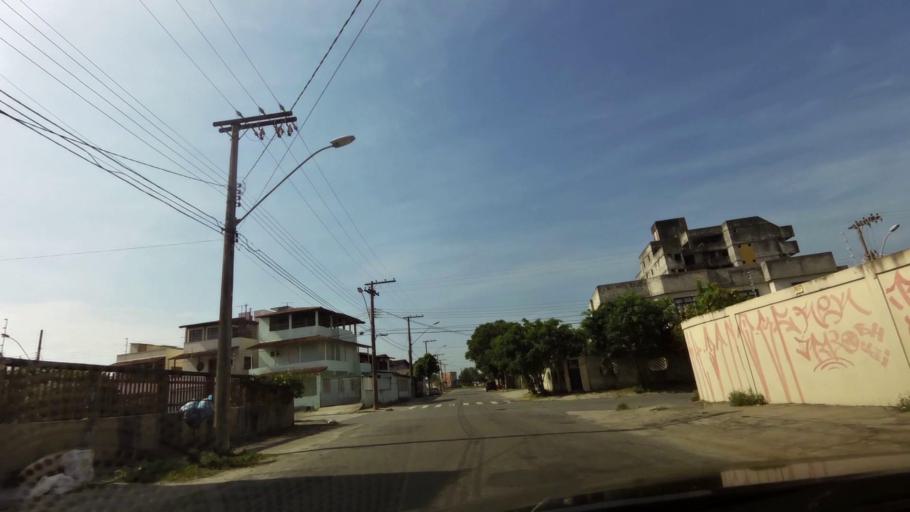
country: BR
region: Espirito Santo
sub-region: Guarapari
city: Guarapari
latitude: -20.6545
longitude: -40.4944
